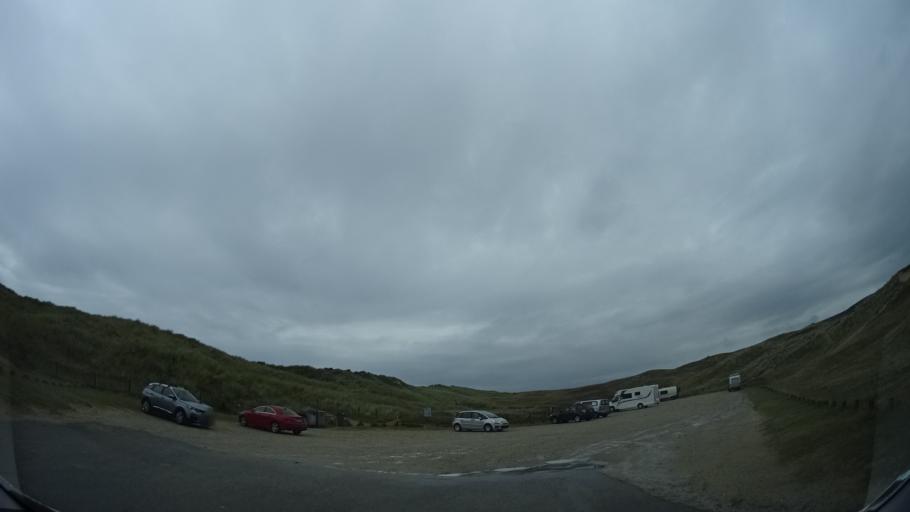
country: FR
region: Lower Normandy
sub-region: Departement de la Manche
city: Beaumont-Hague
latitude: 49.6090
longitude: -1.8412
